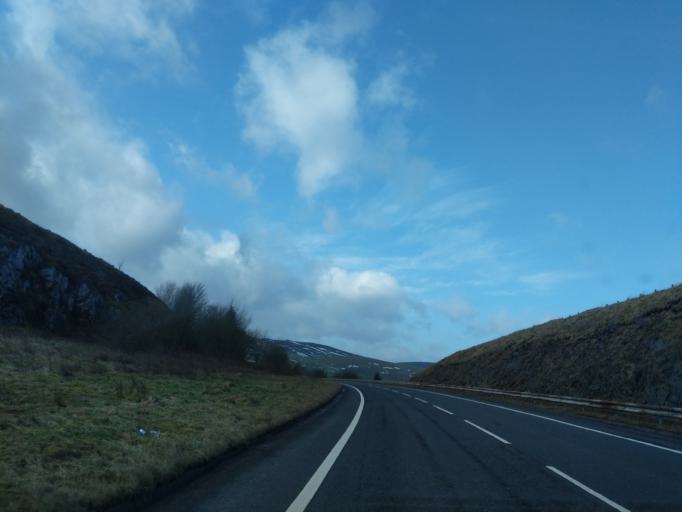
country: GB
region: Scotland
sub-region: South Lanarkshire
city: Biggar
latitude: 55.4684
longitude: -3.6589
